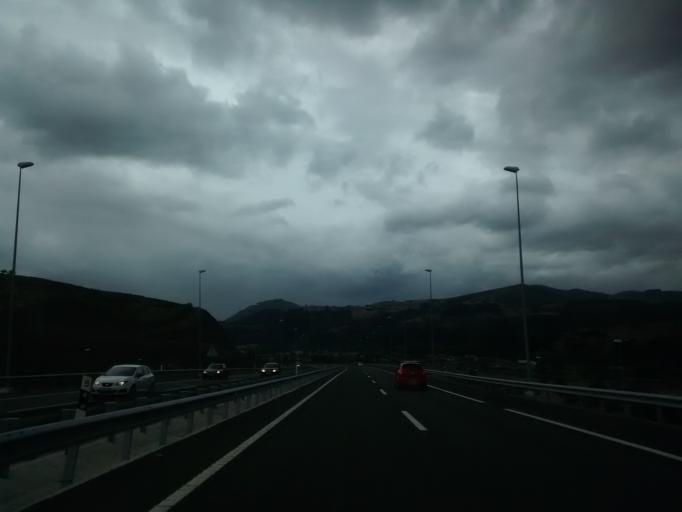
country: ES
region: Cantabria
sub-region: Provincia de Cantabria
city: Molledo
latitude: 43.1631
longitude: -4.0528
